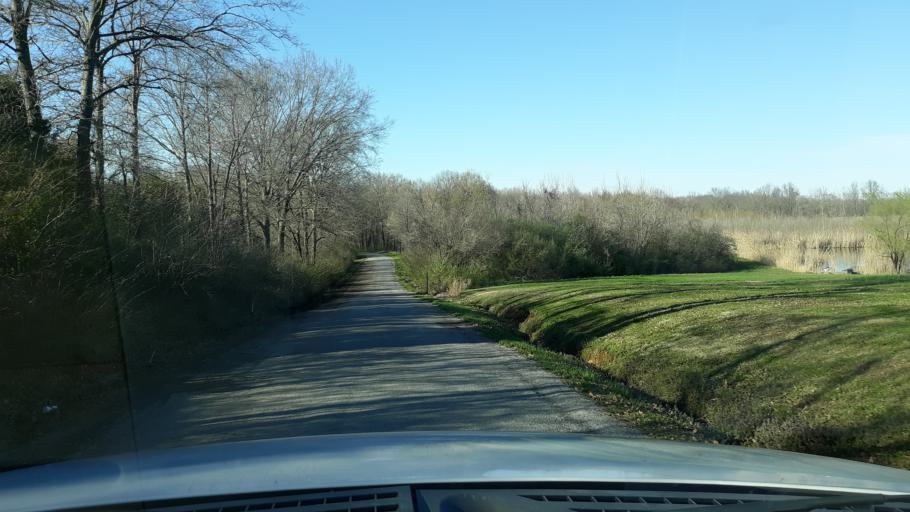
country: US
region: Illinois
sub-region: Saline County
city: Harrisburg
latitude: 37.7552
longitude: -88.5680
